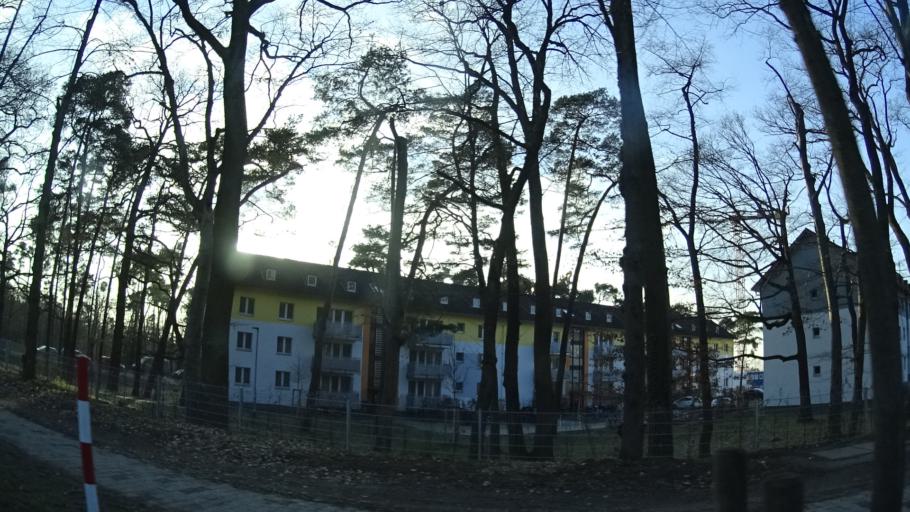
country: DE
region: Hesse
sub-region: Regierungsbezirk Darmstadt
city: Darmstadt
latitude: 49.8437
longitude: 8.6459
